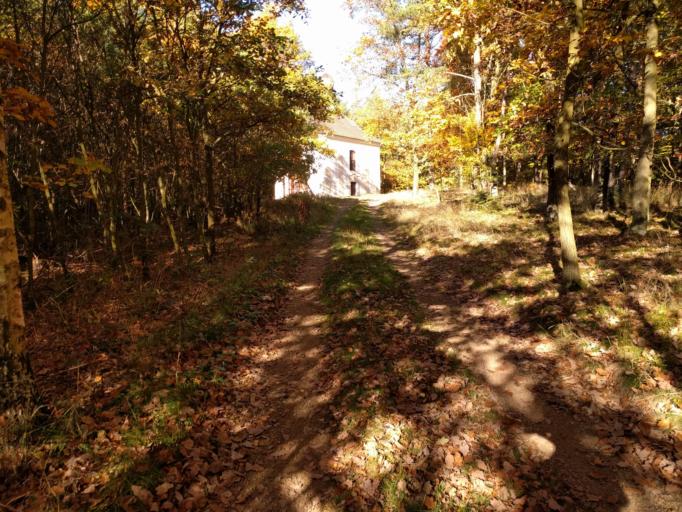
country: CZ
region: Plzensky
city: Zbiroh
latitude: 49.9009
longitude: 13.7191
